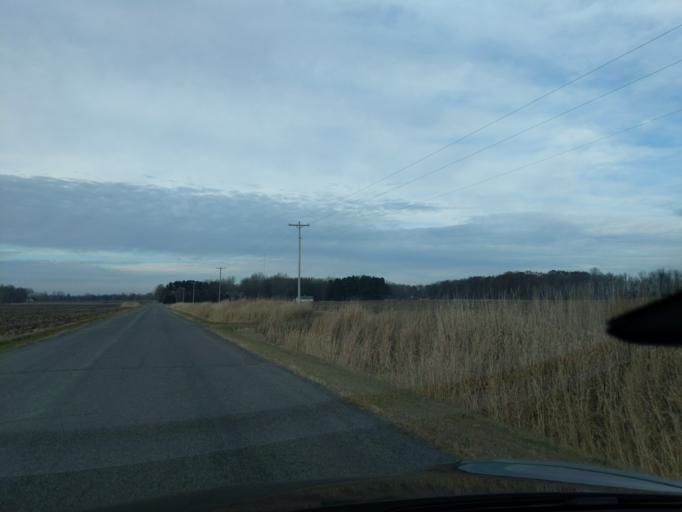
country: US
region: Michigan
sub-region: Ingham County
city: Okemos
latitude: 42.6614
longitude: -84.3835
